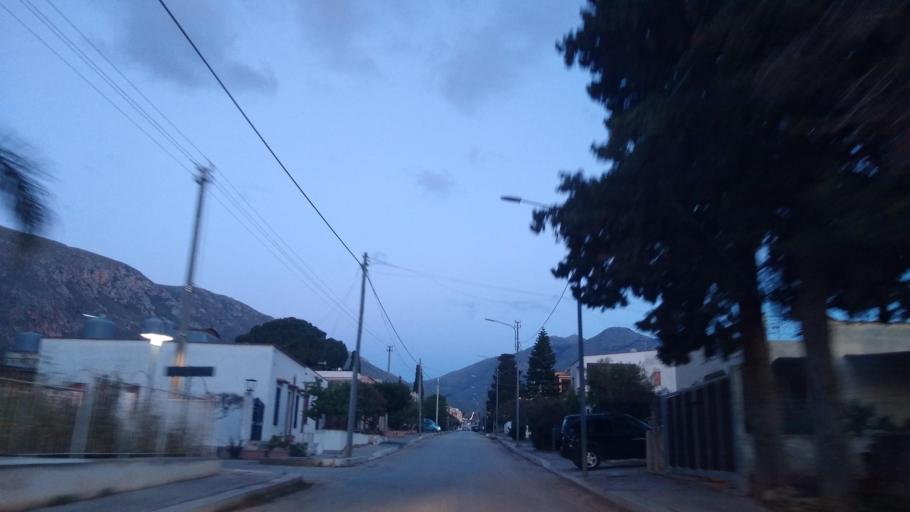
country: IT
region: Sicily
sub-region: Trapani
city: Castelluzzo
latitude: 38.1041
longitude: 12.7322
